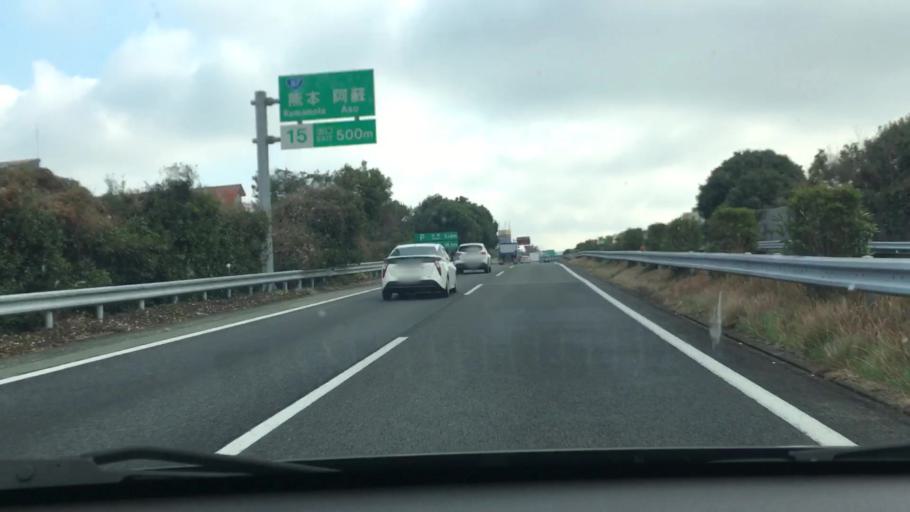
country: JP
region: Kumamoto
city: Kumamoto
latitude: 32.8408
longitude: 130.7749
